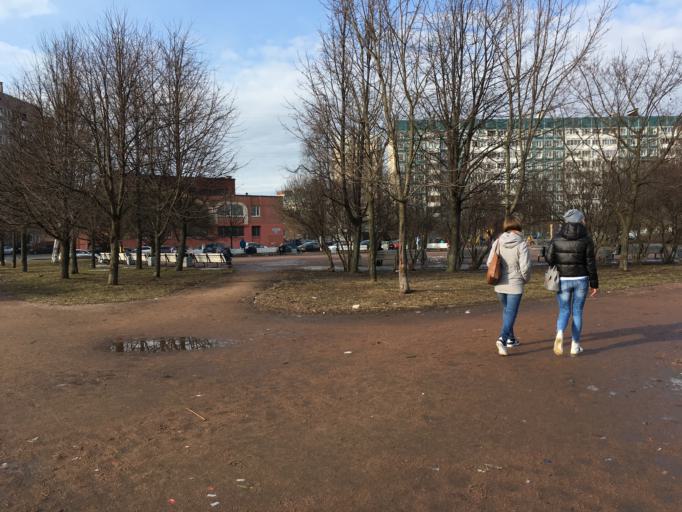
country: RU
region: St.-Petersburg
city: Komendantsky aerodrom
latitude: 60.0178
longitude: 30.2511
